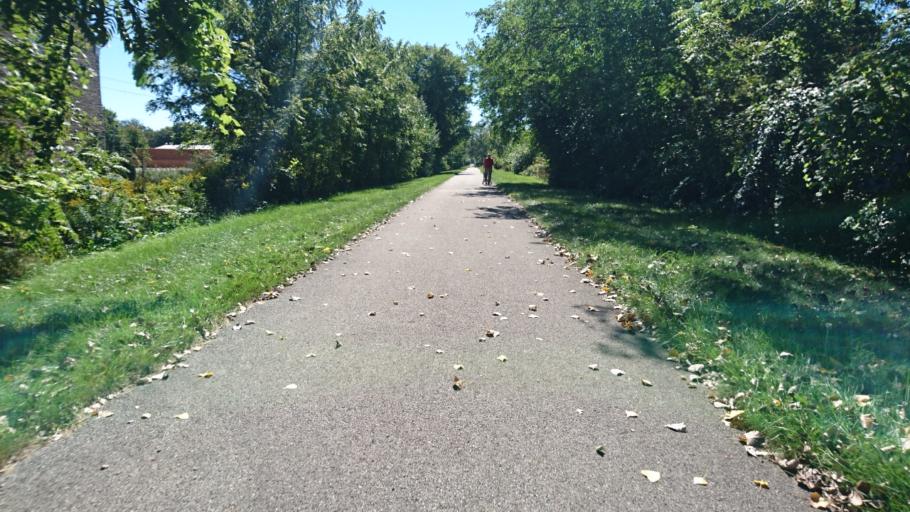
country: US
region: Illinois
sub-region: Cook County
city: Lansing
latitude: 41.5740
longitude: -87.5437
